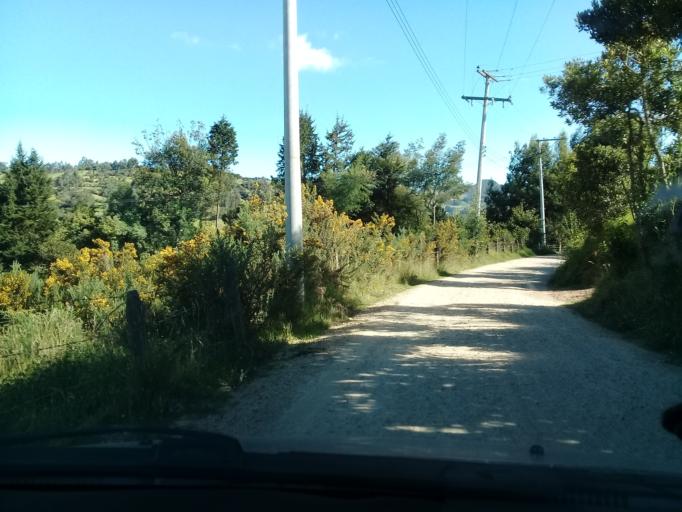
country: CO
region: Cundinamarca
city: Zipaquira
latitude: 5.0024
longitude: -74.0693
